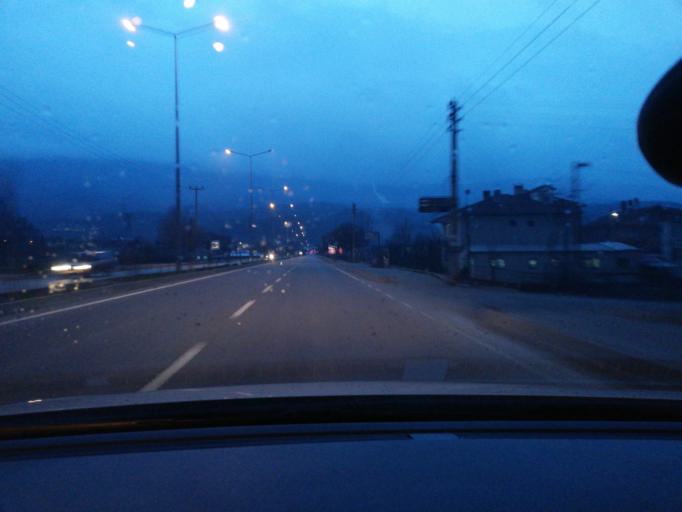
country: TR
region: Bolu
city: Bolu
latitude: 40.6970
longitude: 31.6188
